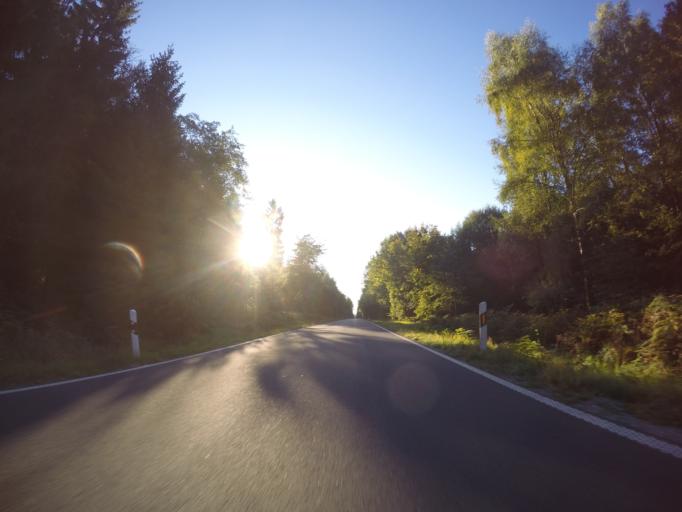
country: DE
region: Bavaria
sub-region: Regierungsbezirk Unterfranken
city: Altenbuch
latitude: 49.8629
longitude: 9.4182
